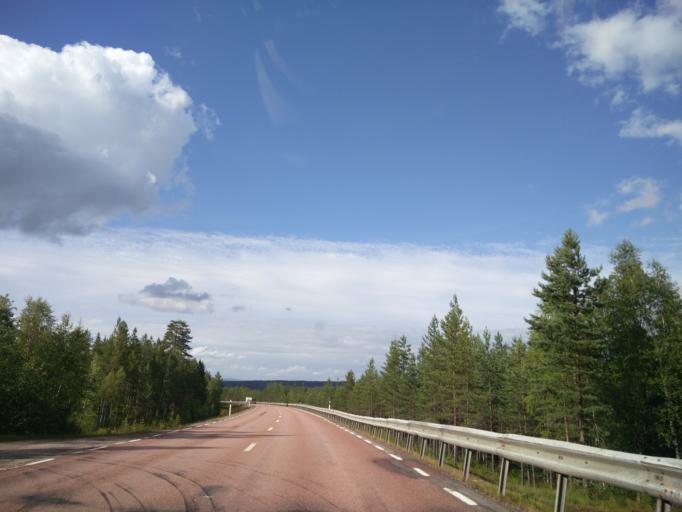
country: SE
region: Vaermland
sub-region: Hagfors Kommun
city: Ekshaerad
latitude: 60.3923
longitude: 13.2625
